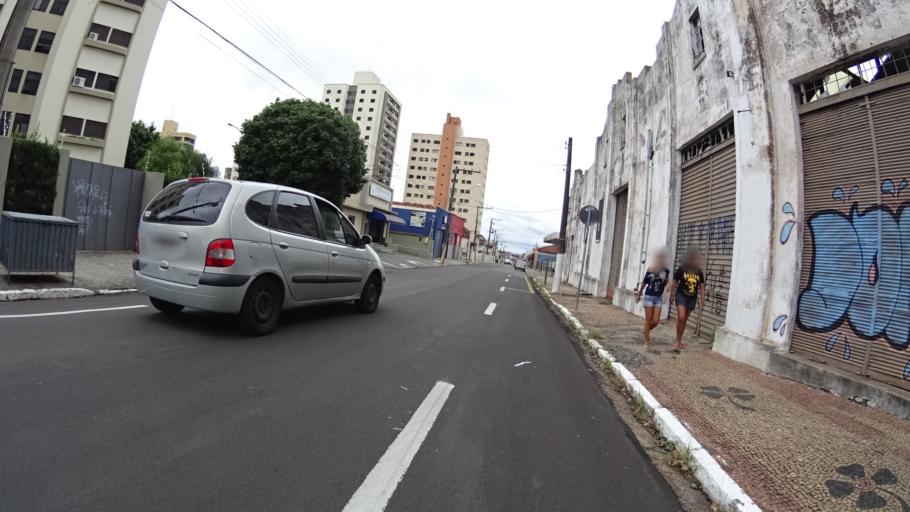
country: BR
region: Sao Paulo
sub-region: Marilia
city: Marilia
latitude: -22.2220
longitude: -49.9575
